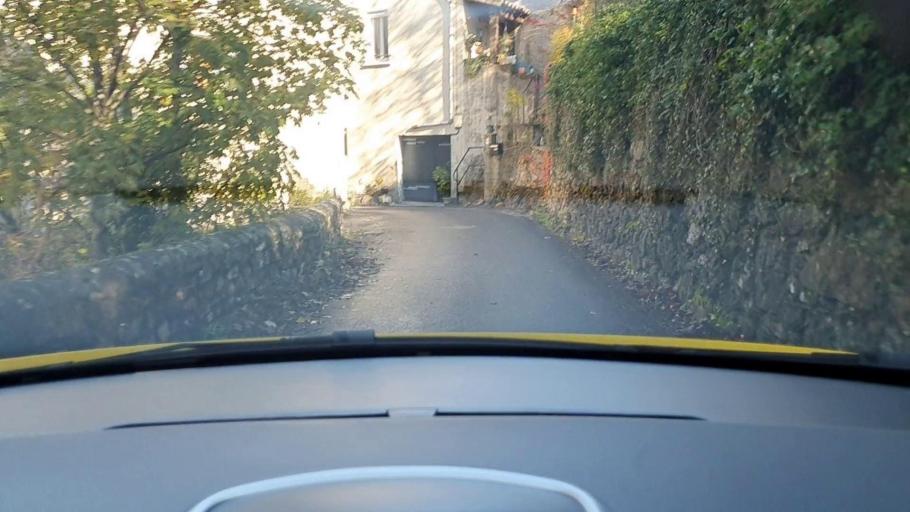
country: FR
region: Languedoc-Roussillon
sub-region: Departement du Gard
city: Le Vigan
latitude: 43.9883
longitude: 3.6076
